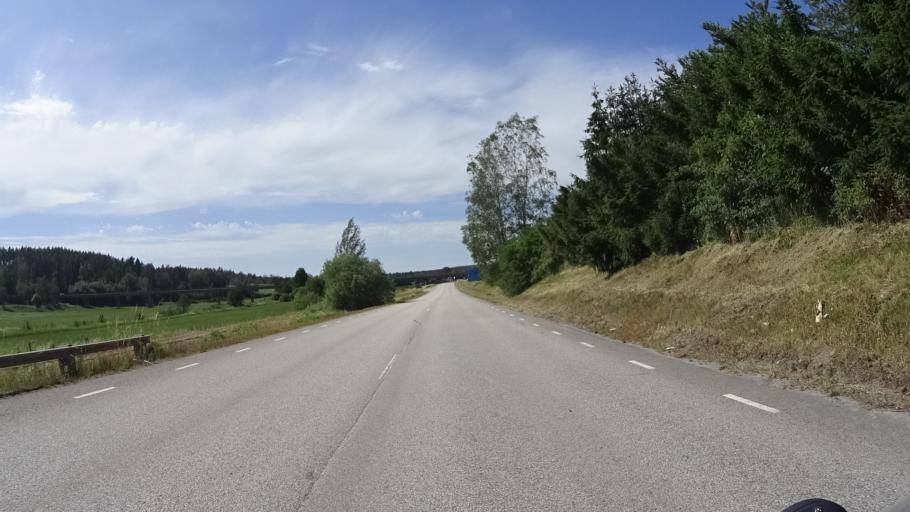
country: SE
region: Kalmar
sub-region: Vasterviks Kommun
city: Gamleby
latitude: 57.9060
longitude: 16.3918
